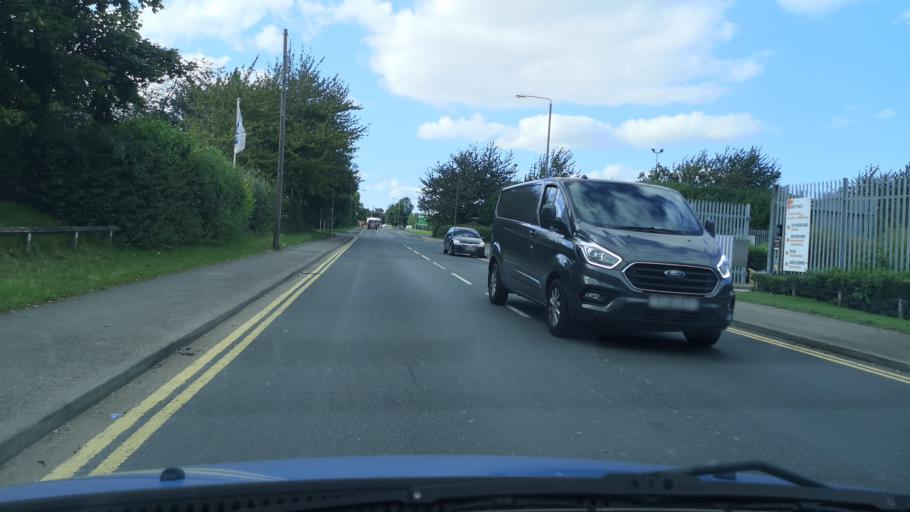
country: GB
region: England
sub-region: City and Borough of Wakefield
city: South Elmsall
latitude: 53.6027
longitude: -1.2744
